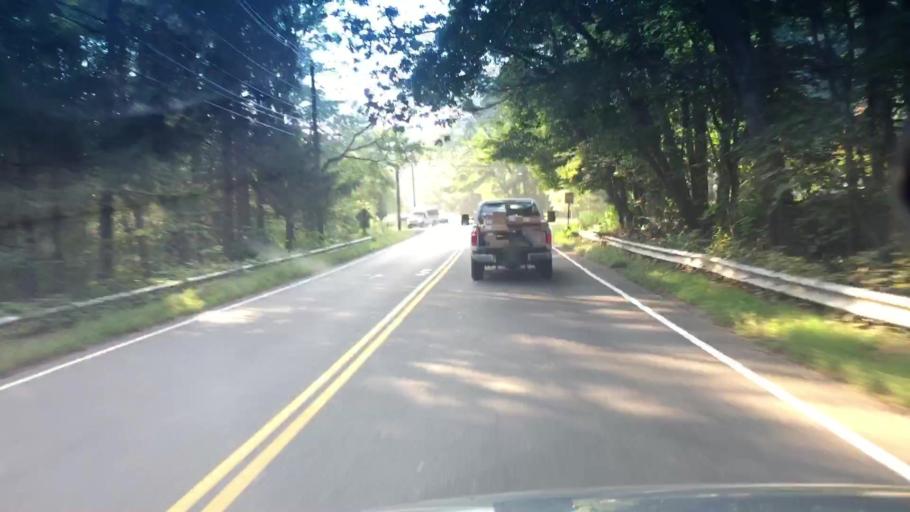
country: US
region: Massachusetts
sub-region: Norfolk County
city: Walpole
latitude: 42.1552
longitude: -71.2701
